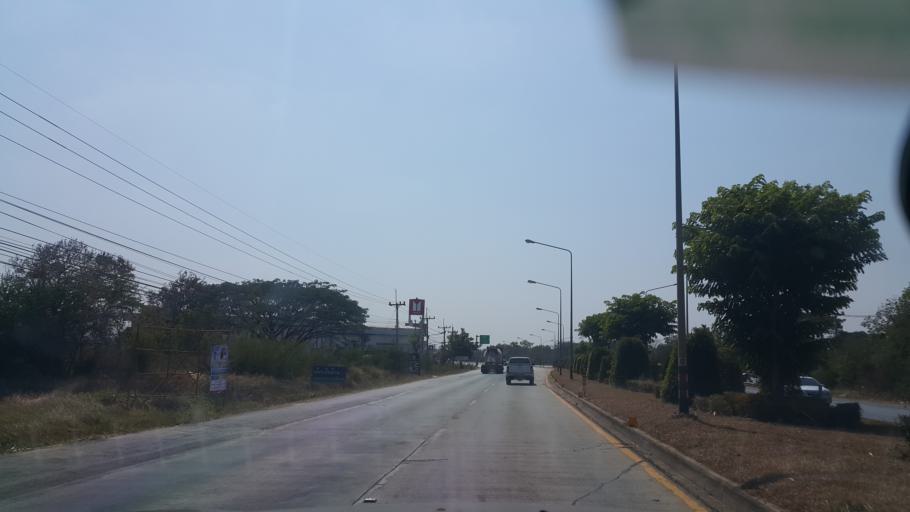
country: TH
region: Khon Kaen
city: Phon
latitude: 15.8368
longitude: 102.6099
